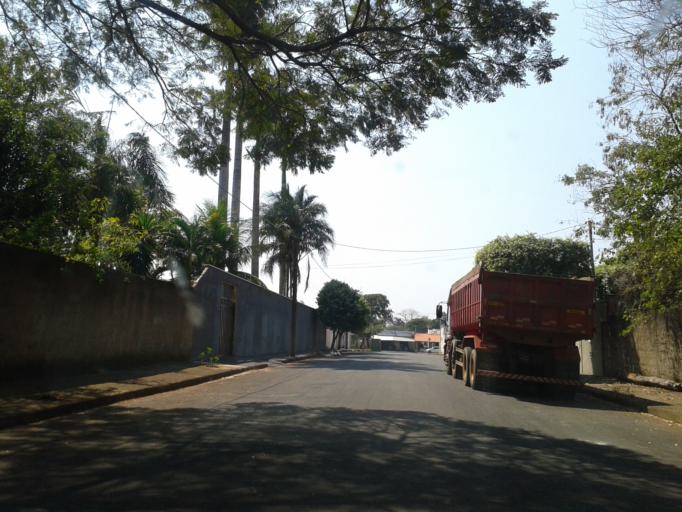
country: BR
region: Minas Gerais
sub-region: Ituiutaba
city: Ituiutaba
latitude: -18.9642
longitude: -49.4535
